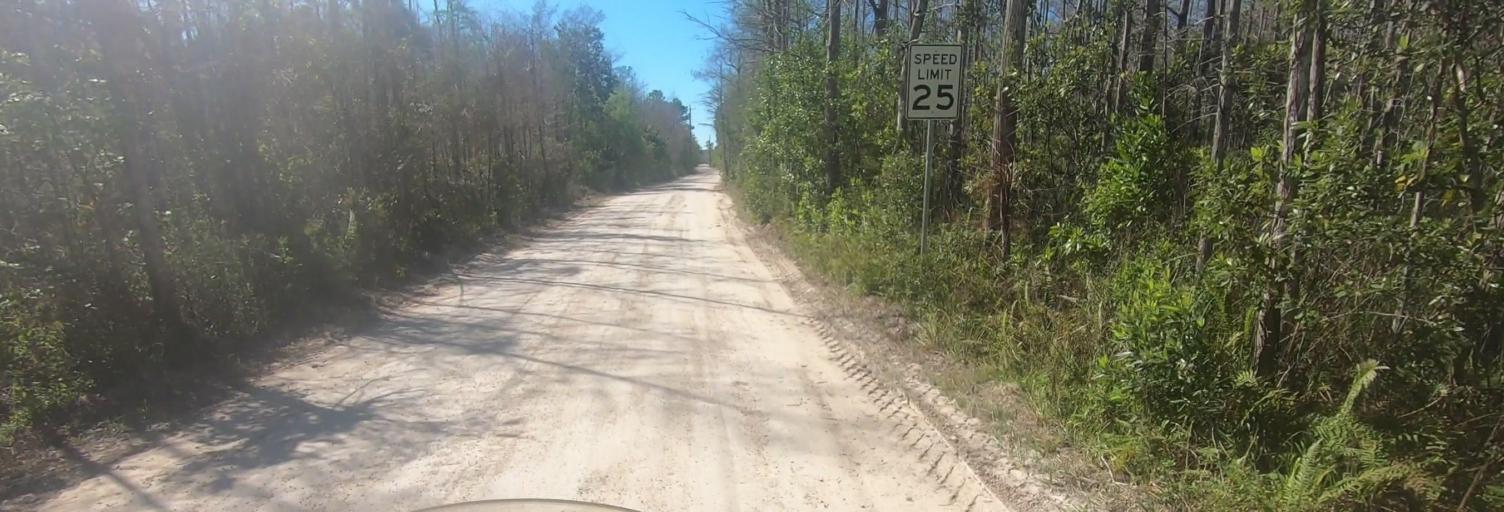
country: US
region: Florida
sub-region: Collier County
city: Lely Resort
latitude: 25.8912
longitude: -81.2299
